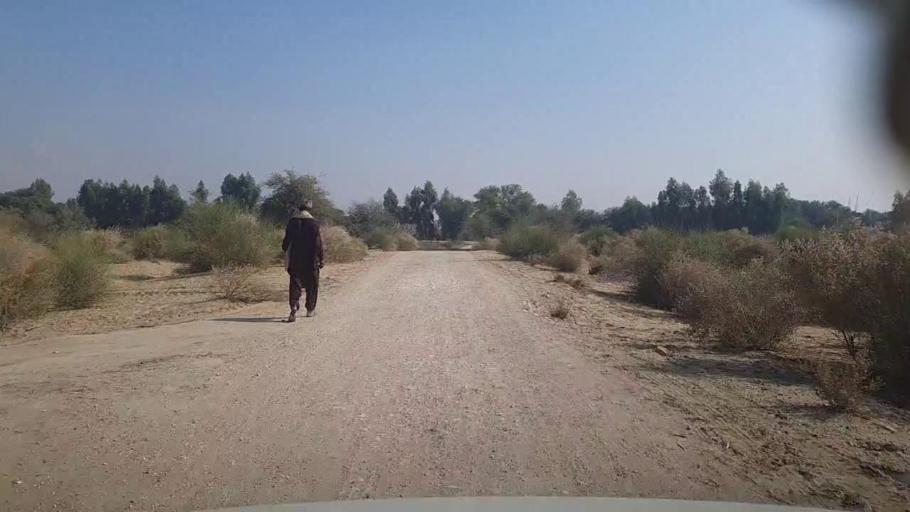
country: PK
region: Sindh
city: Kandiari
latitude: 26.9380
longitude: 68.5500
